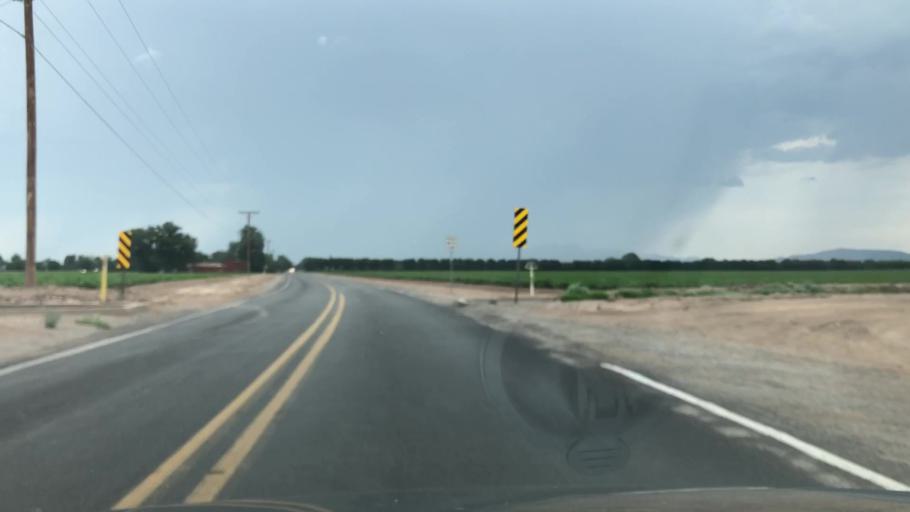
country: US
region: New Mexico
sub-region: Dona Ana County
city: La Union
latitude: 31.9740
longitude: -106.6516
